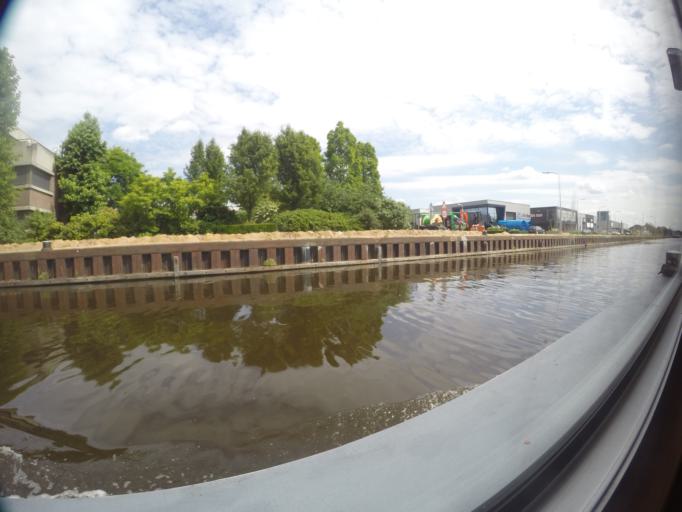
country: NL
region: Overijssel
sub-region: Gemeente Hengelo
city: Hengelo
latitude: 52.2497
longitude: 6.7738
